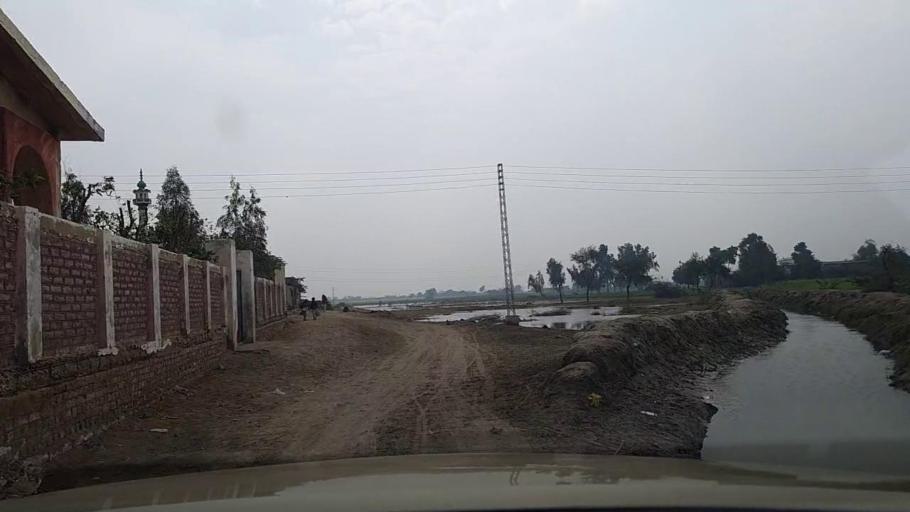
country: PK
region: Sindh
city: Sanghar
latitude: 26.1161
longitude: 68.9163
